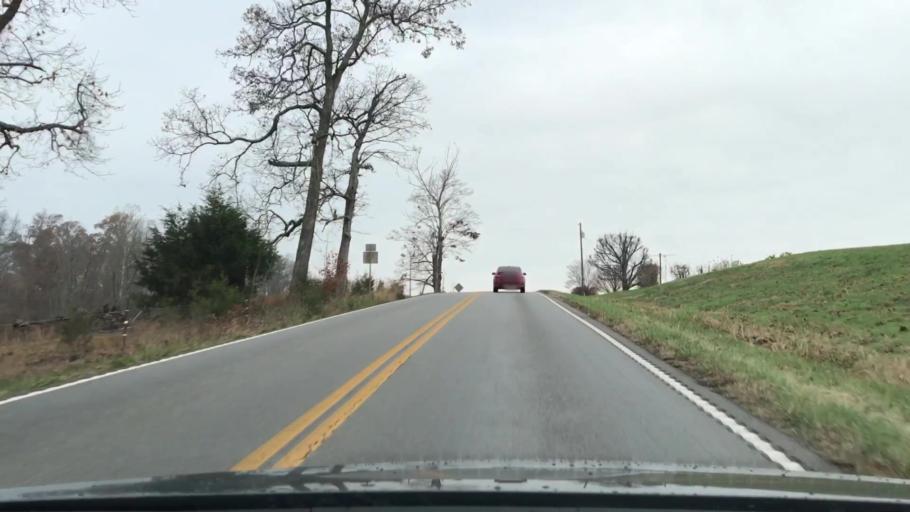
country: US
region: Tennessee
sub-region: Sumner County
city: Portland
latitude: 36.7056
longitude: -86.4203
